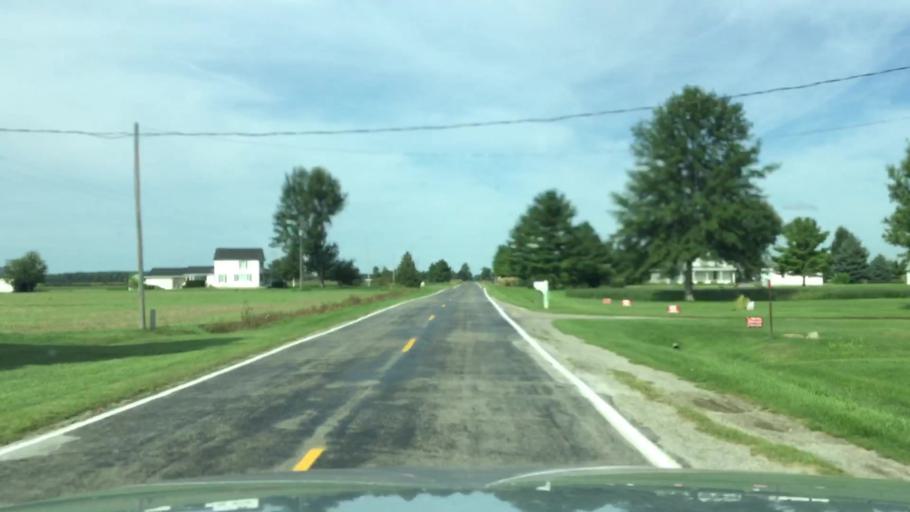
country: US
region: Michigan
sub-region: Genesee County
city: Montrose
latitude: 43.1466
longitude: -83.9981
